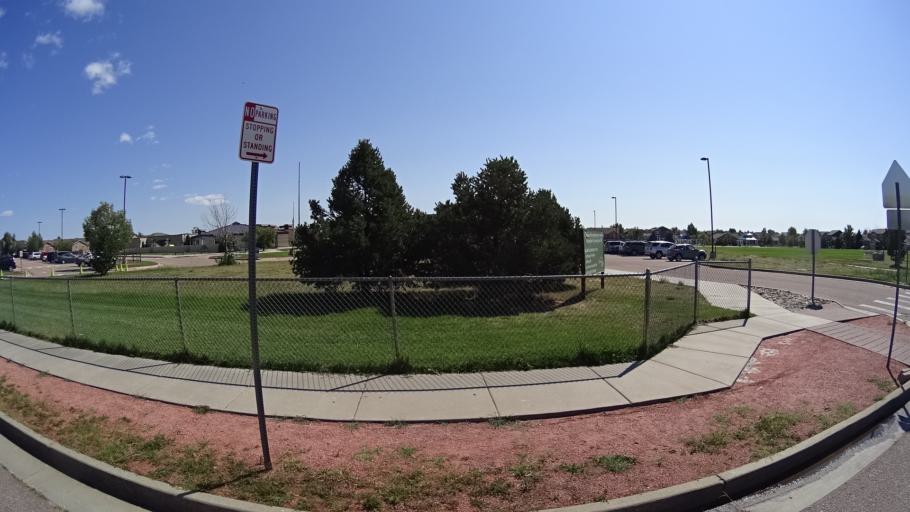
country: US
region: Colorado
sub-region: El Paso County
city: Cimarron Hills
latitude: 38.9212
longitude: -104.7012
